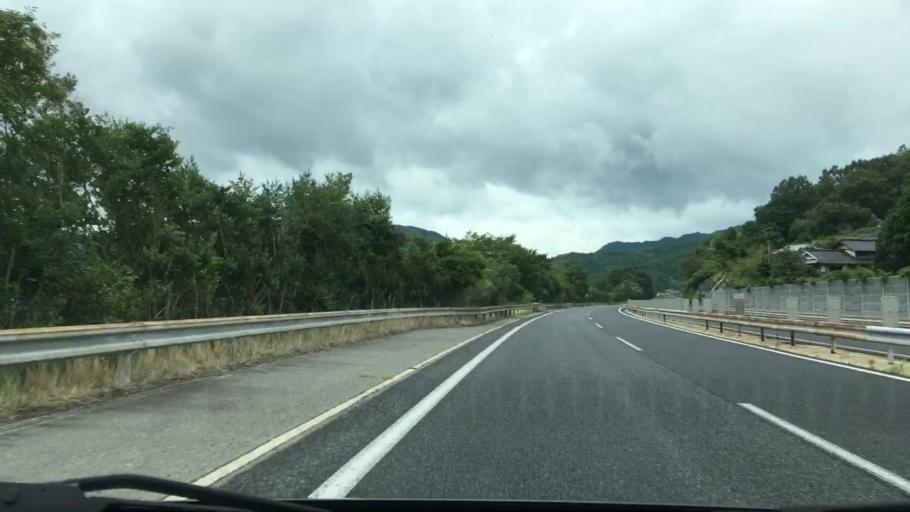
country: JP
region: Okayama
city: Takahashi
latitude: 34.9861
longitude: 133.7055
